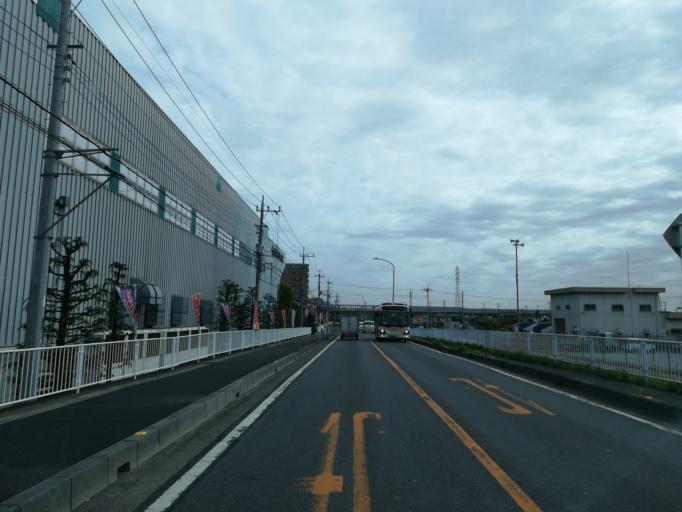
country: JP
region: Saitama
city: Satte
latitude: 36.0621
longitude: 139.7053
